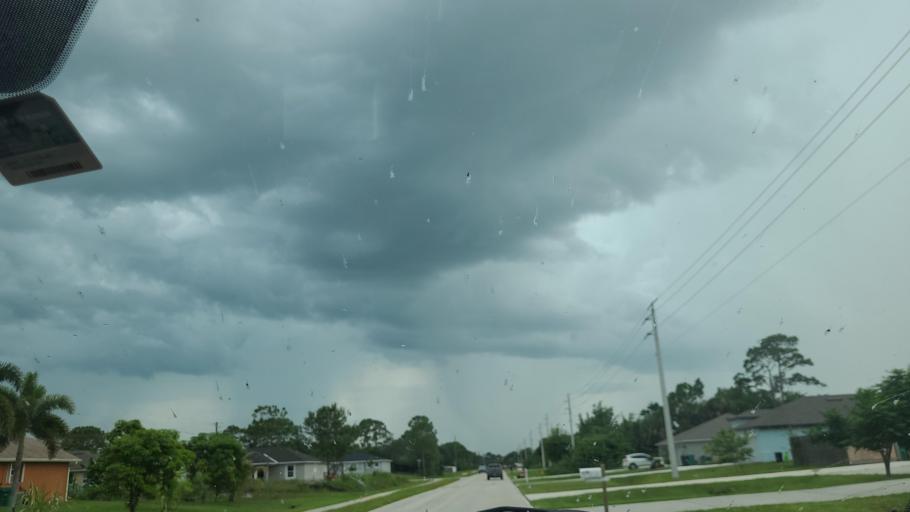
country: US
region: Florida
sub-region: Saint Lucie County
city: Port Saint Lucie
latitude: 27.2144
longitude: -80.3835
